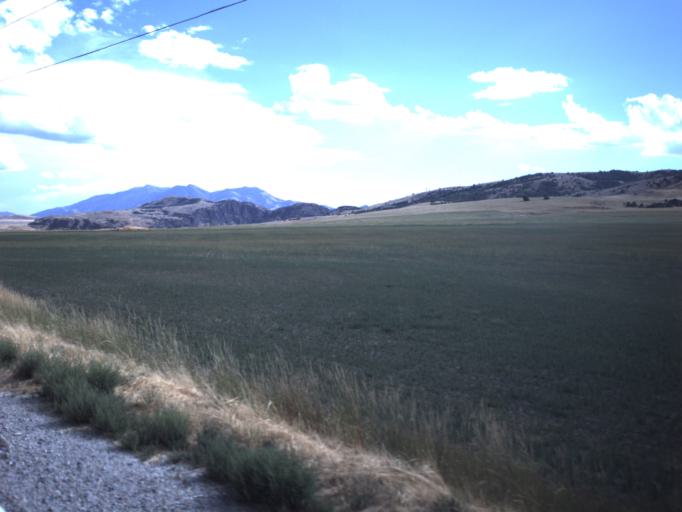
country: US
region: Utah
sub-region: Cache County
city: Benson
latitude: 41.8913
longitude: -112.0401
